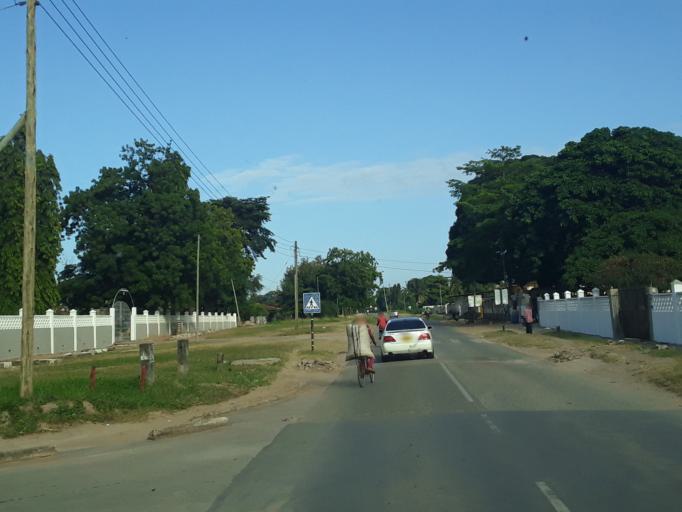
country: TZ
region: Tanga
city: Tanga
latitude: -5.0728
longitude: 39.1104
